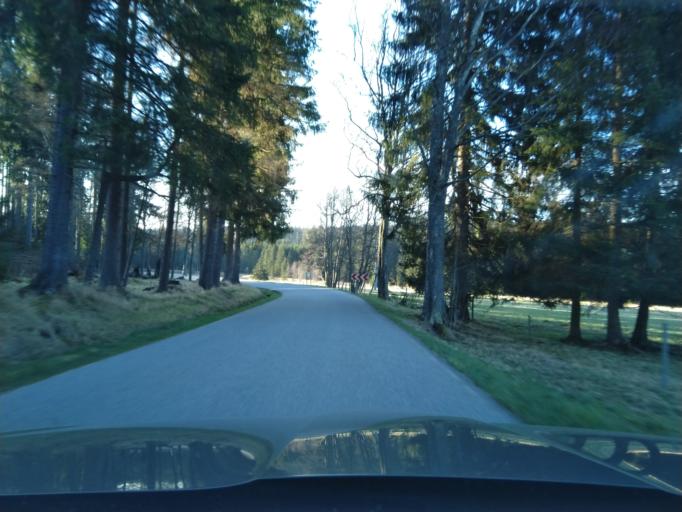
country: DE
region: Bavaria
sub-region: Lower Bavaria
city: Haidmuhle
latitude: 48.8677
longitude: 13.7926
